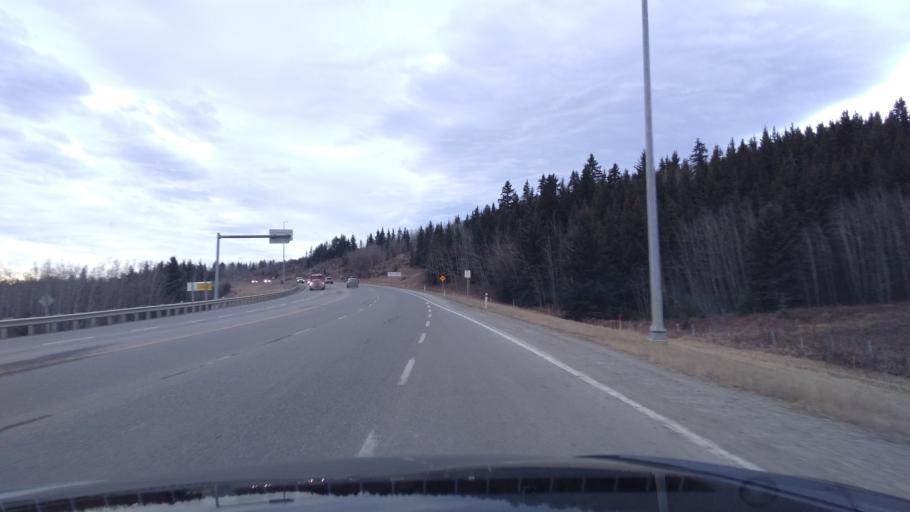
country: CA
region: Alberta
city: Cochrane
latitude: 51.1802
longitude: -114.4878
